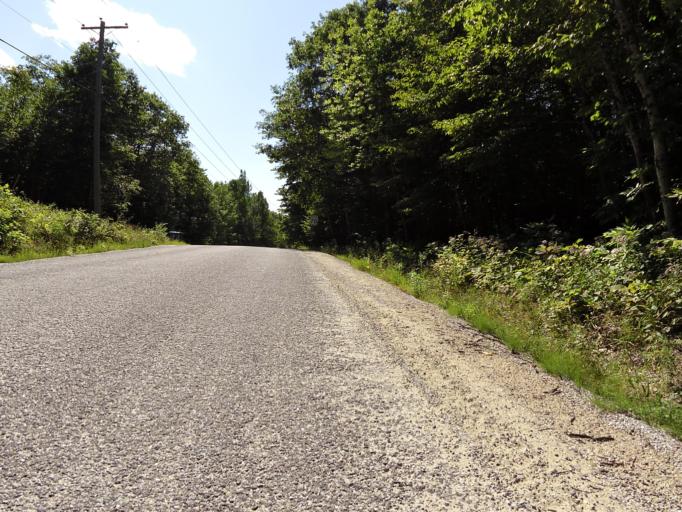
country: CA
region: Quebec
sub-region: Outaouais
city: Maniwaki
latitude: 46.2148
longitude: -76.0728
